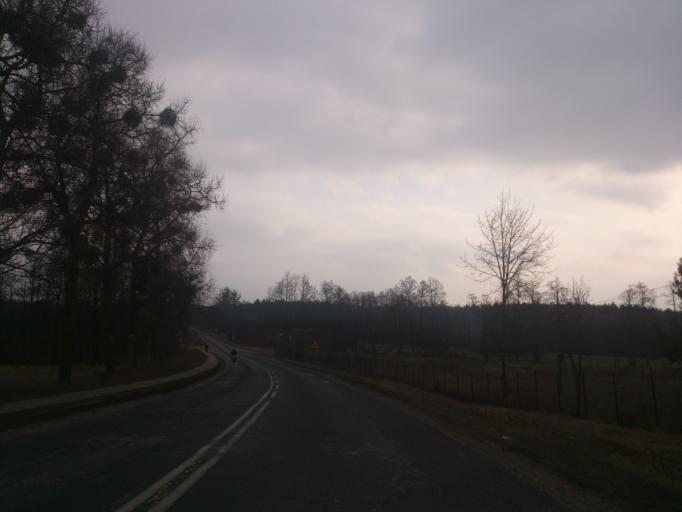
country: PL
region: Kujawsko-Pomorskie
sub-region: Powiat golubsko-dobrzynski
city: Golub-Dobrzyn
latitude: 53.0948
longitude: 19.0473
